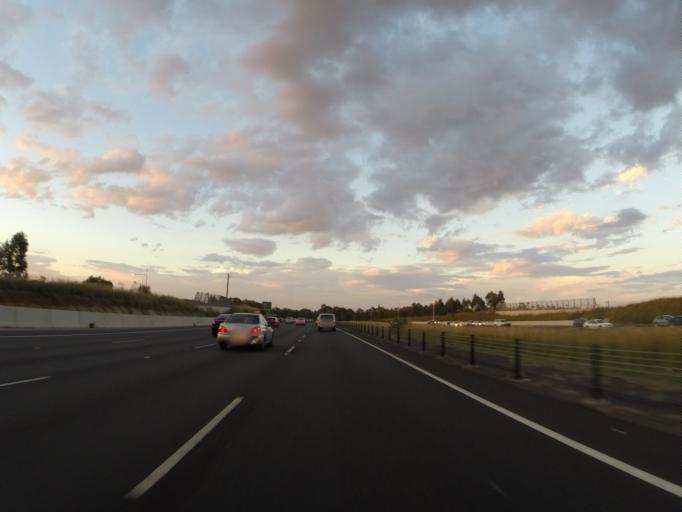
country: AU
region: New South Wales
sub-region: Campbelltown Municipality
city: Glenfield
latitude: -33.9727
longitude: 150.8729
